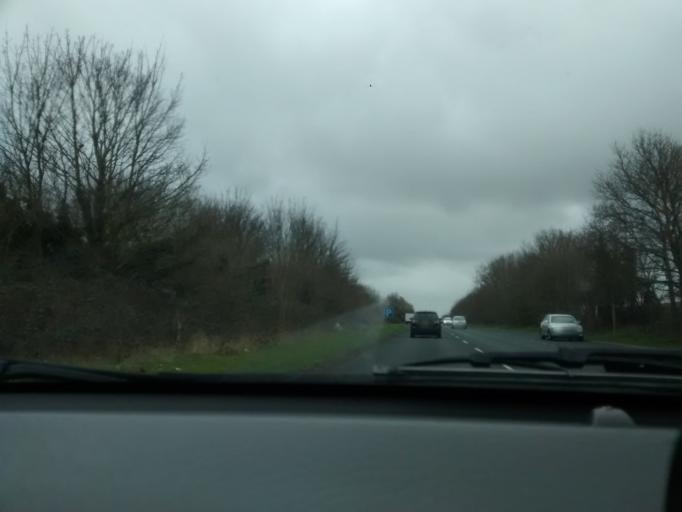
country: GB
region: England
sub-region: Suffolk
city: Felixstowe
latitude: 51.9735
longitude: 1.3442
